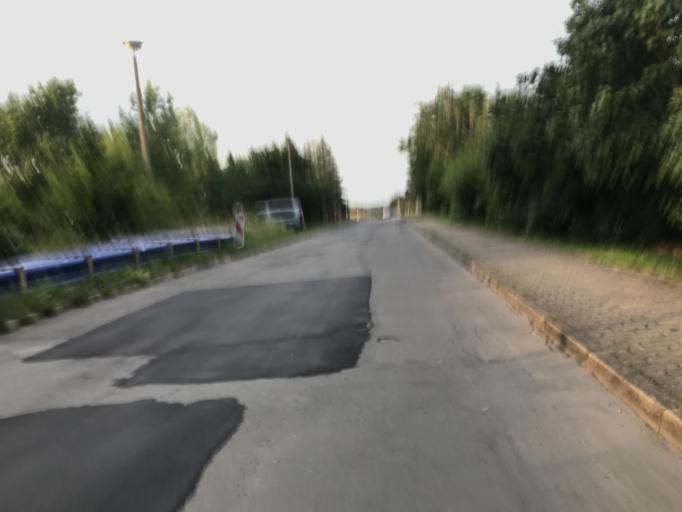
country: DE
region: Saxony-Anhalt
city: Quedlinburg
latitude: 51.7994
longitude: 11.1573
